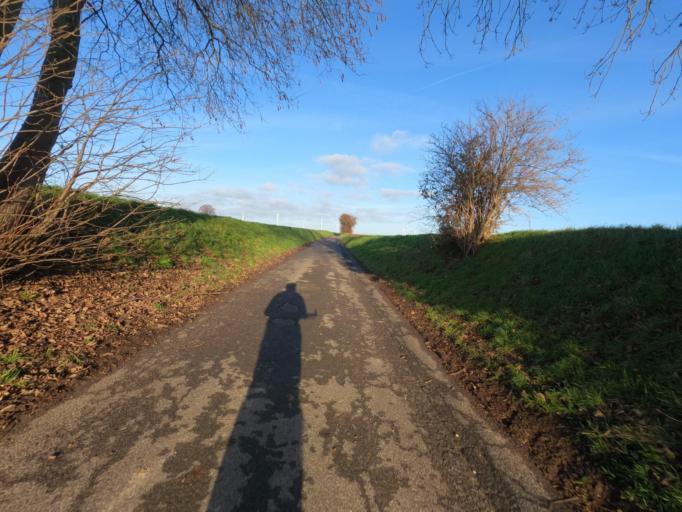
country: DE
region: North Rhine-Westphalia
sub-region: Regierungsbezirk Koln
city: Elsdorf
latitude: 50.9611
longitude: 6.5020
